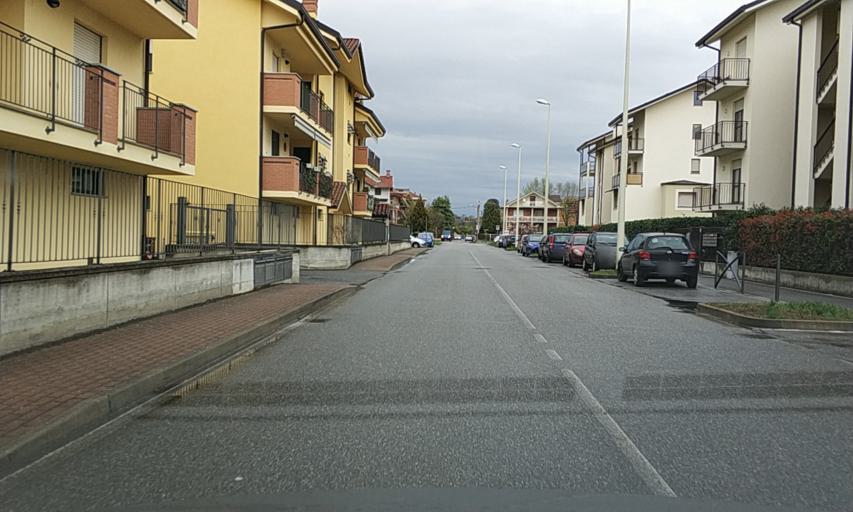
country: IT
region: Piedmont
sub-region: Provincia di Torino
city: Cirie
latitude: 45.2385
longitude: 7.5876
